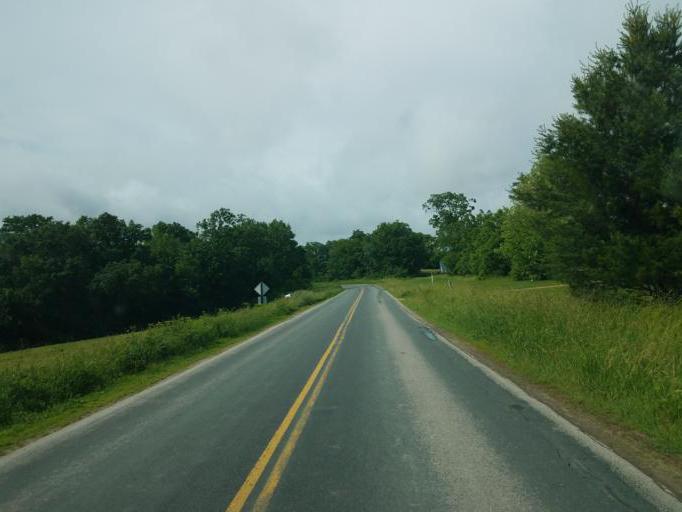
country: US
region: Wisconsin
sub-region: Juneau County
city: Elroy
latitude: 43.8113
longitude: -90.4314
